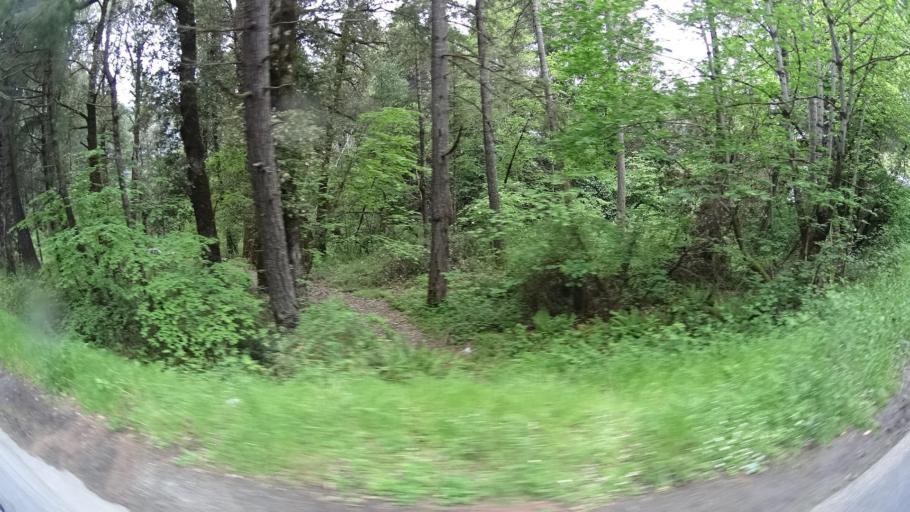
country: US
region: California
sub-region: Humboldt County
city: Willow Creek
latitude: 41.0577
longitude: -123.6735
